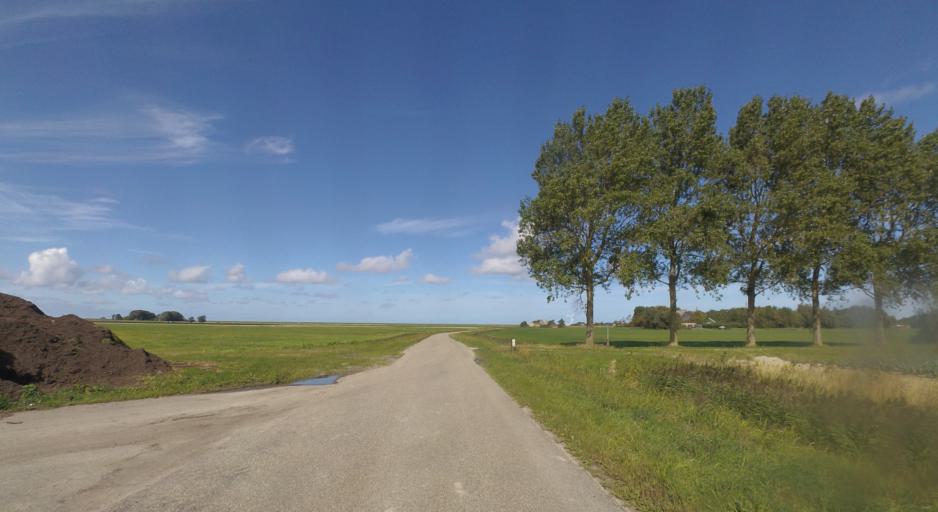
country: NL
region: Friesland
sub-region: Gemeente Dongeradeel
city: Holwerd
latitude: 53.3610
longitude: 5.8968
